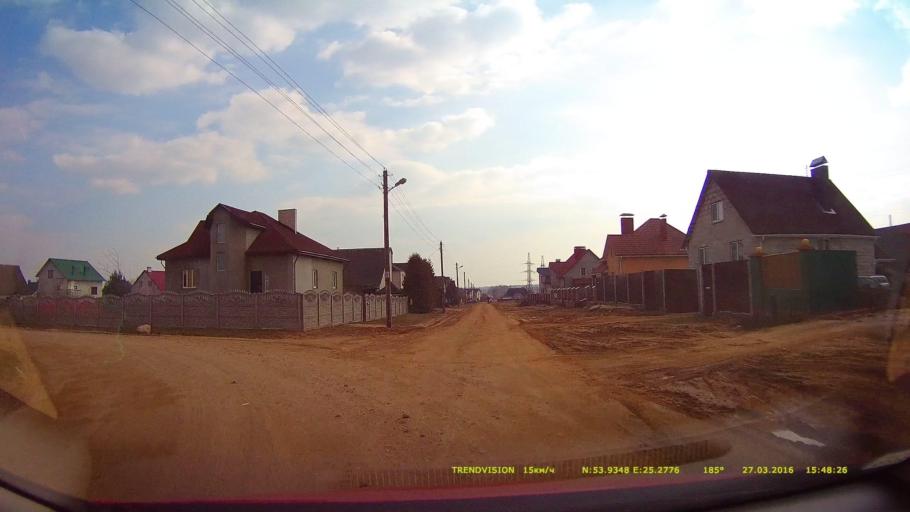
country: BY
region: Grodnenskaya
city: Lida
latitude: 53.9350
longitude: 25.2777
